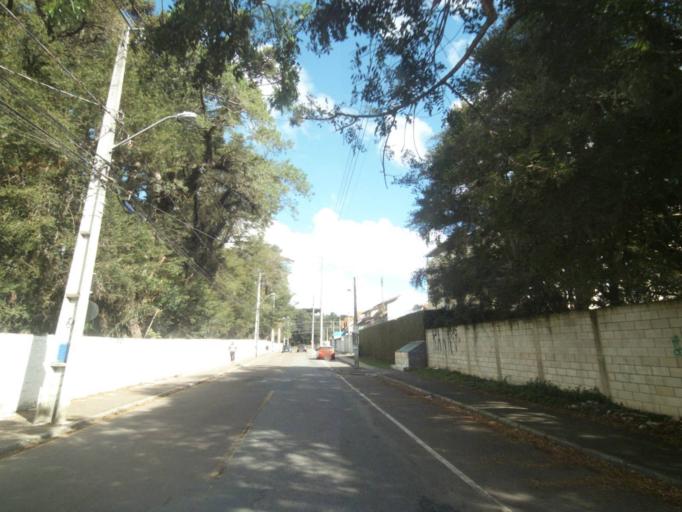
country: BR
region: Parana
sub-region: Sao Jose Dos Pinhais
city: Sao Jose dos Pinhais
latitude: -25.5330
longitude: -49.2921
